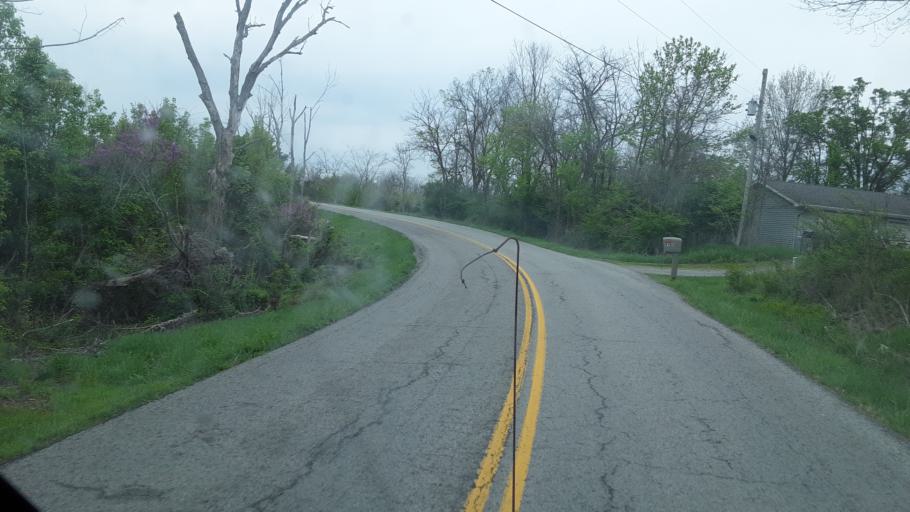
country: US
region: Kentucky
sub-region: Grant County
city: Dry Ridge
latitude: 38.6611
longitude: -84.6962
